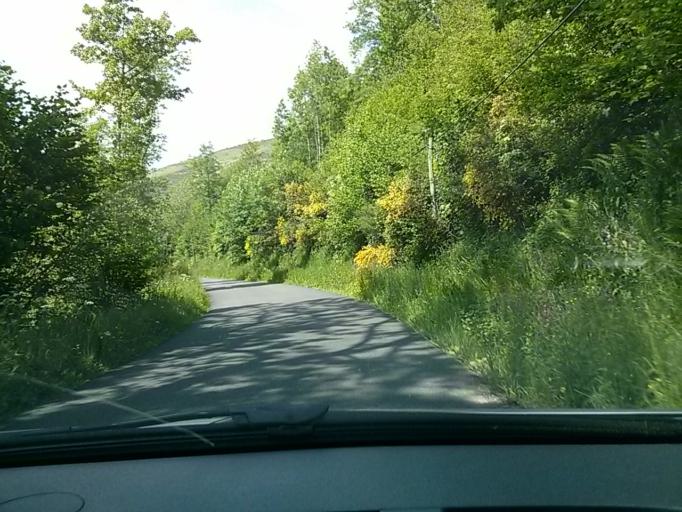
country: FR
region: Rhone-Alpes
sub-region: Departement de la Loire
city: Saint-Chamond
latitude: 45.4082
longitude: 4.5398
